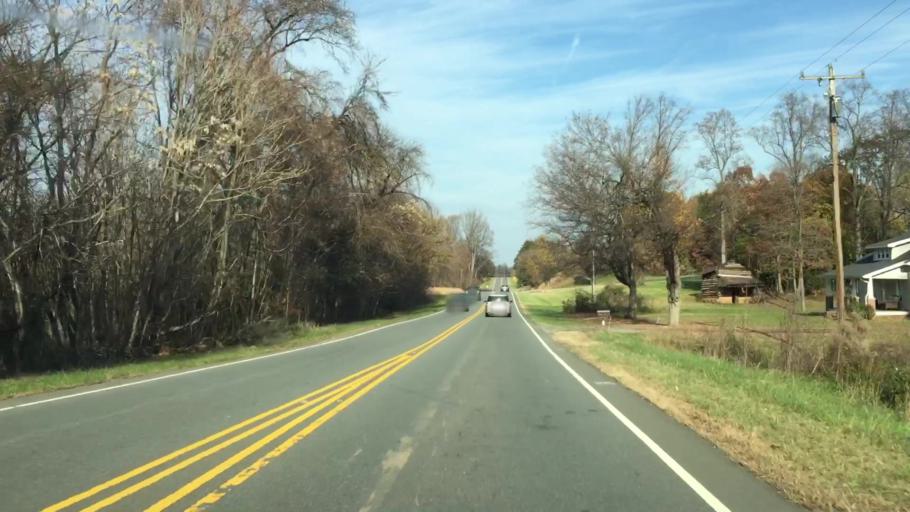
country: US
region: North Carolina
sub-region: Forsyth County
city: Walkertown
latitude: 36.1742
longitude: -80.1272
